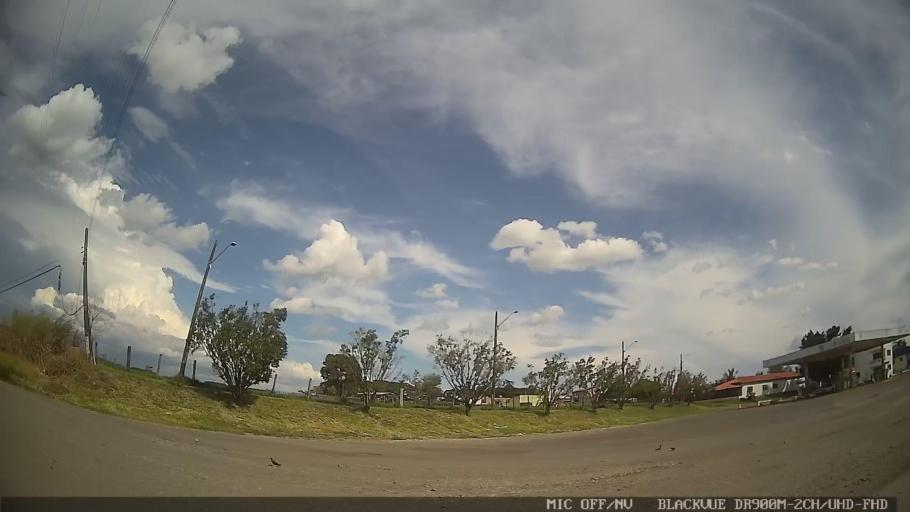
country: BR
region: Sao Paulo
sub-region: Conchas
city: Conchas
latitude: -23.0602
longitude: -47.9665
